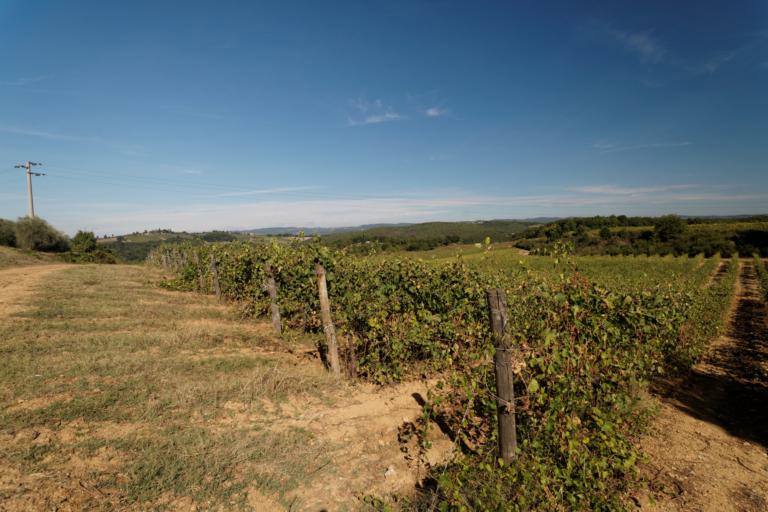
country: IT
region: Tuscany
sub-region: Provincia di Siena
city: Monteriggioni
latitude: 43.3897
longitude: 11.2257
